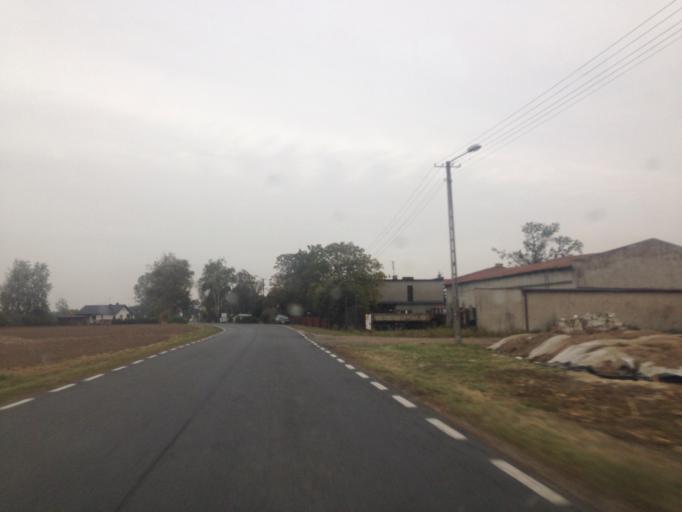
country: PL
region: Greater Poland Voivodeship
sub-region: Powiat poznanski
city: Kleszczewo
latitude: 52.3561
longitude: 17.1184
